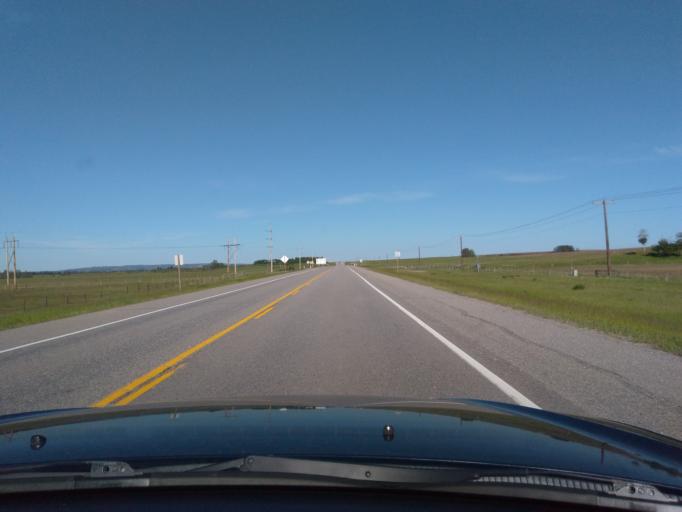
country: CA
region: Alberta
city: Cochrane
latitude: 51.0235
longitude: -114.4589
